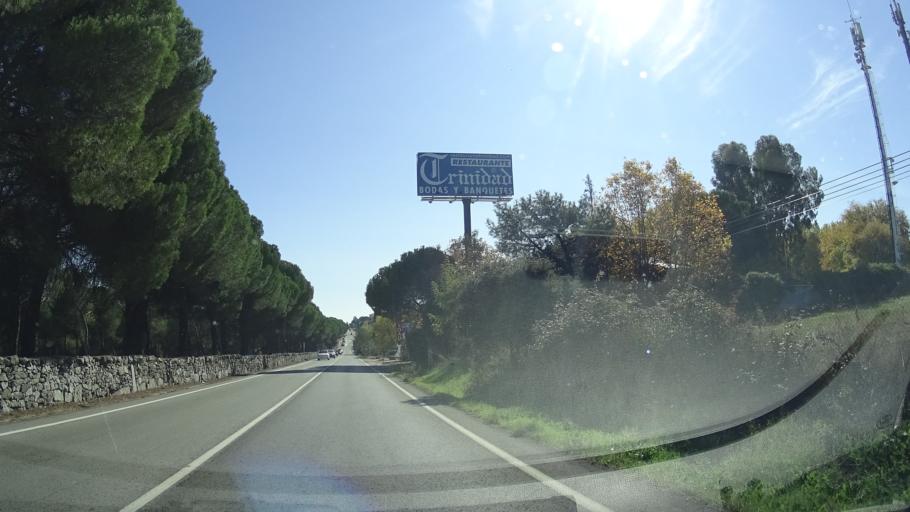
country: ES
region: Madrid
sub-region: Provincia de Madrid
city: Galapagar
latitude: 40.5611
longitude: -3.9681
